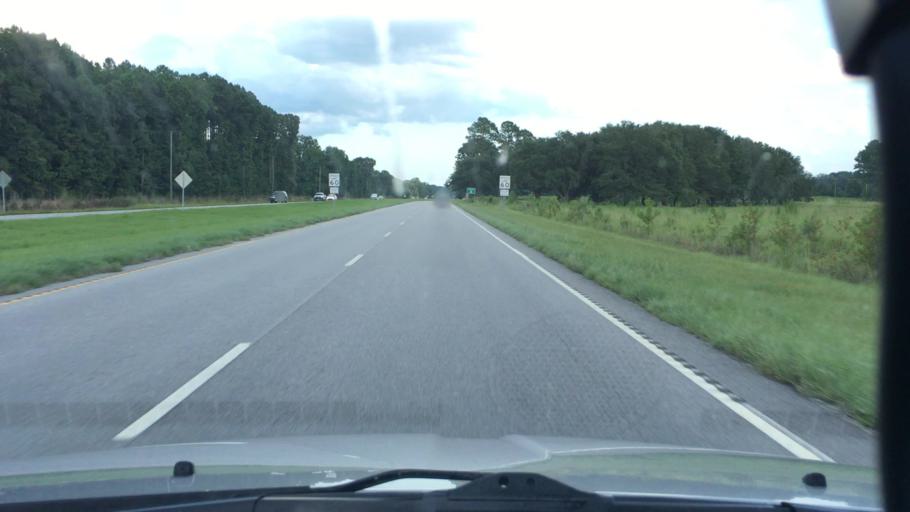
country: US
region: South Carolina
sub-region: Hampton County
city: Yemassee
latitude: 32.6383
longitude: -80.8469
